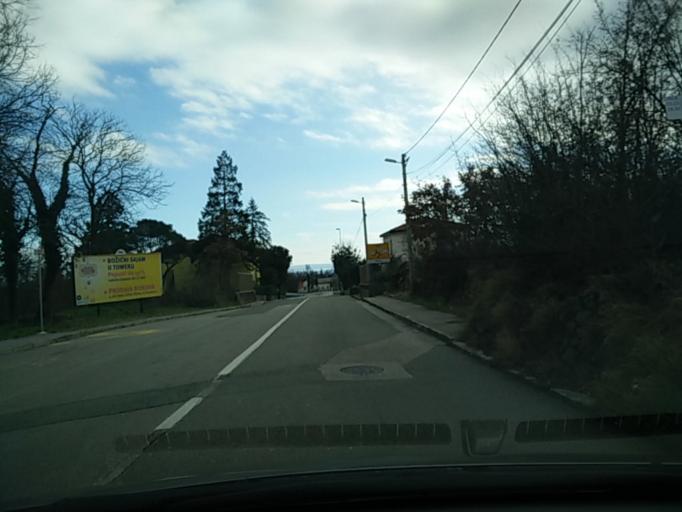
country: HR
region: Primorsko-Goranska
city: Matulji
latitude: 45.3658
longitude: 14.3120
